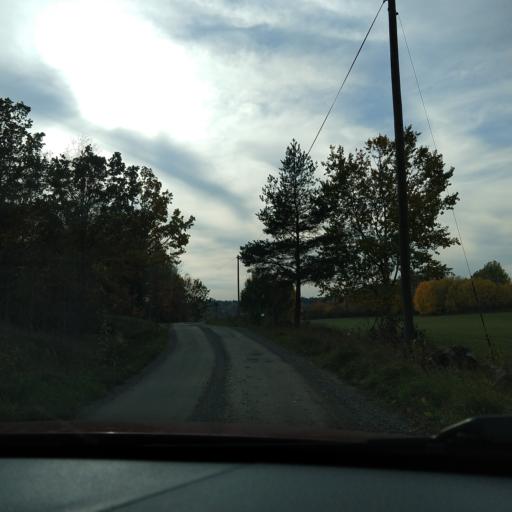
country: SE
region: Stockholm
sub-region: Vallentuna Kommun
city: Vallentuna
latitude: 59.5317
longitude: 18.0087
